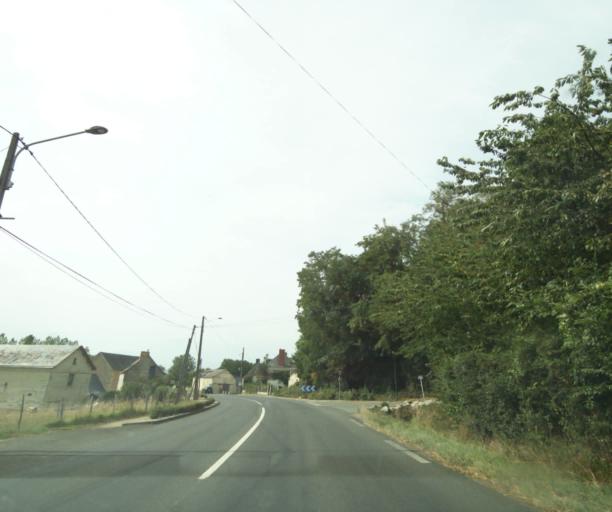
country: FR
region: Centre
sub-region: Departement d'Indre-et-Loire
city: Saint-Christophe-sur-le-Nais
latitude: 47.6622
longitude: 0.4760
